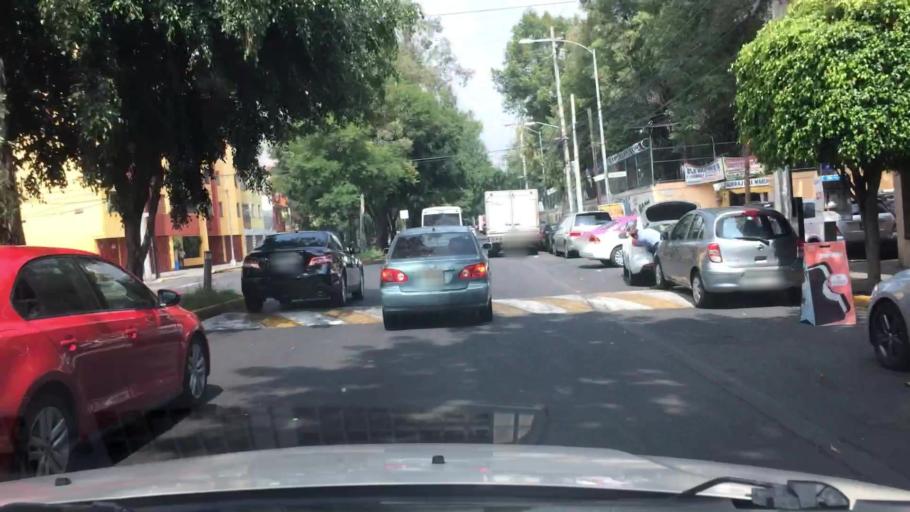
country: MX
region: Mexico City
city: Coyoacan
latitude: 19.3415
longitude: -99.1541
